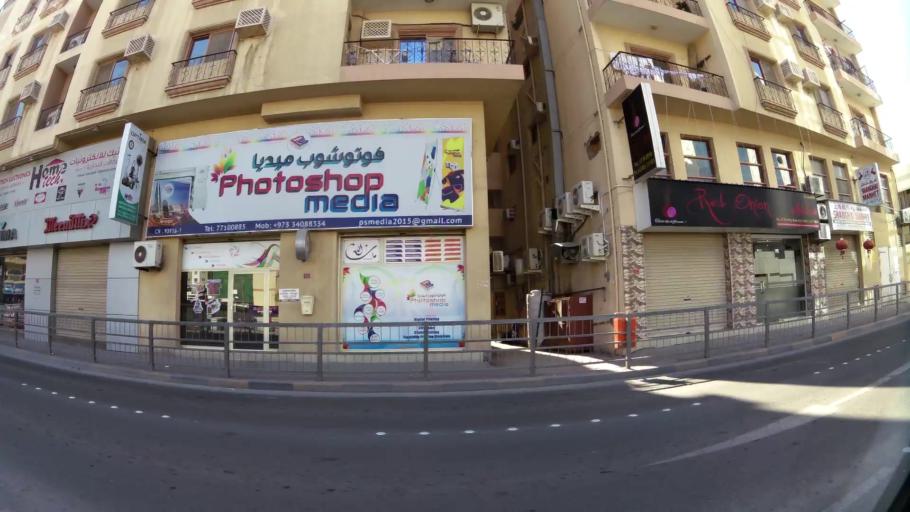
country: BH
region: Manama
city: Manama
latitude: 26.2283
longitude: 50.5821
